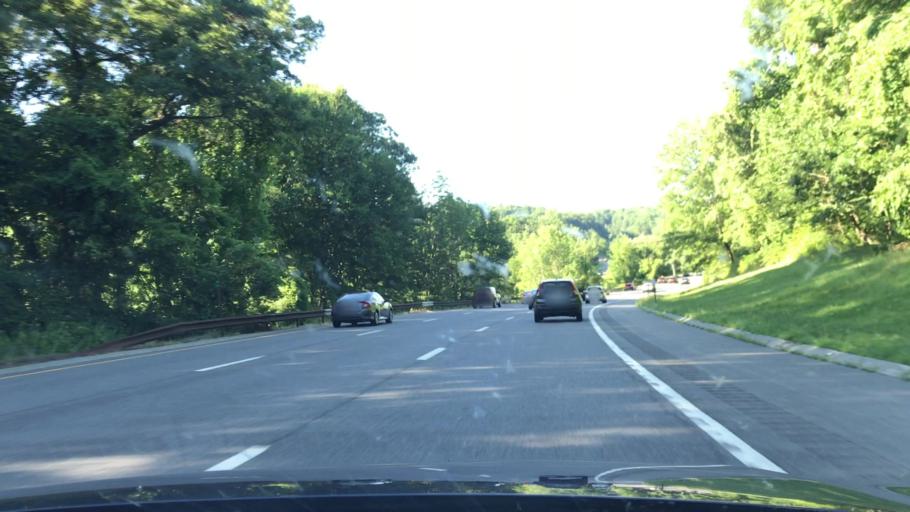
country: US
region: New York
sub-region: Westchester County
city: Yorktown Heights
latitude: 41.2459
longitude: -73.8138
